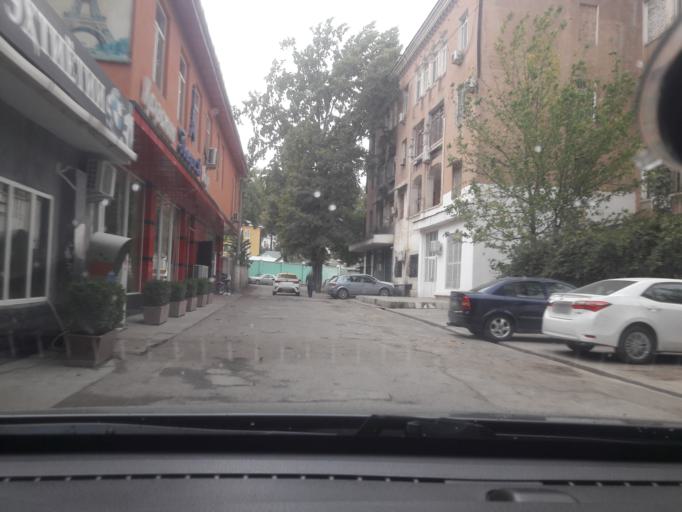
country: TJ
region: Dushanbe
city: Dushanbe
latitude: 38.5640
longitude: 68.7908
